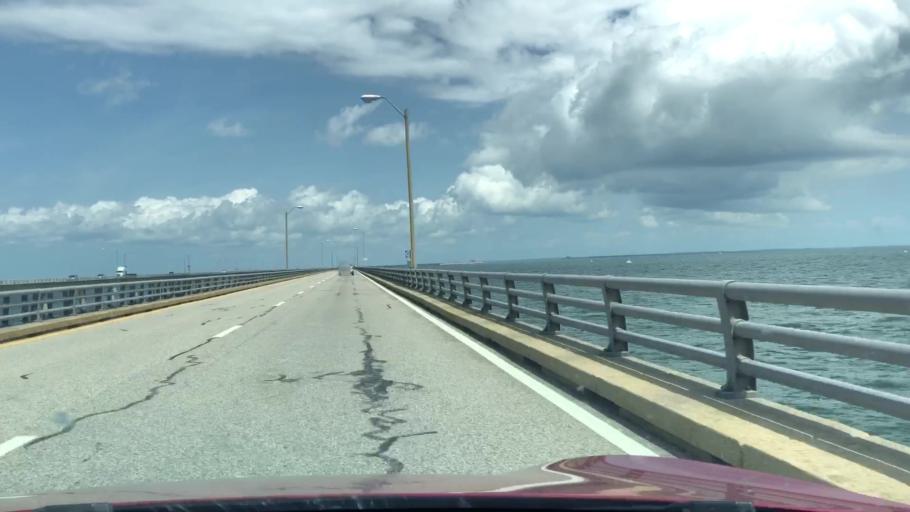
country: US
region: Virginia
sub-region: City of Virginia Beach
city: Virginia Beach
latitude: 37.0048
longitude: -76.0966
